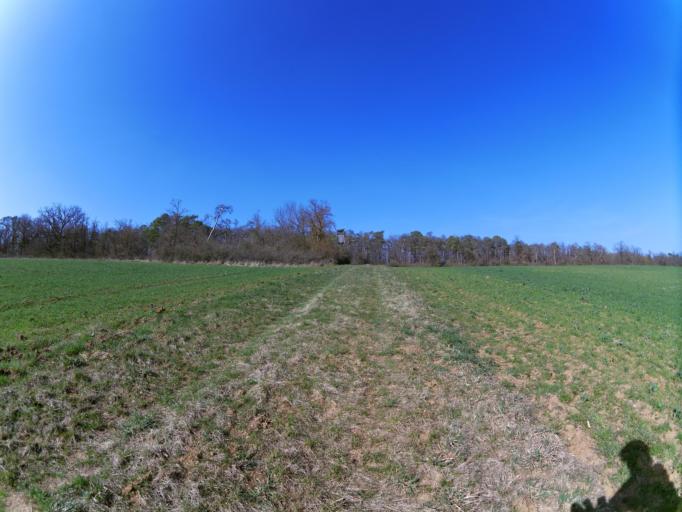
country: DE
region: Bavaria
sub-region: Regierungsbezirk Unterfranken
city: Greussenheim
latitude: 49.8060
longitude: 9.7605
